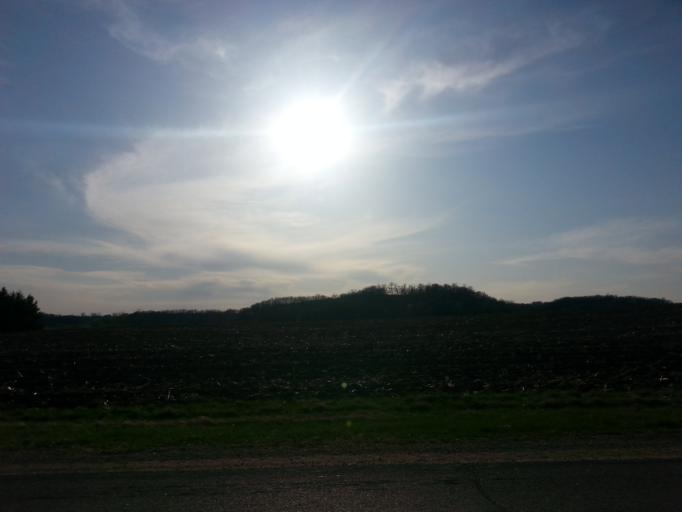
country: US
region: Wisconsin
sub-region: Pierce County
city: River Falls
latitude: 44.7707
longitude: -92.6398
